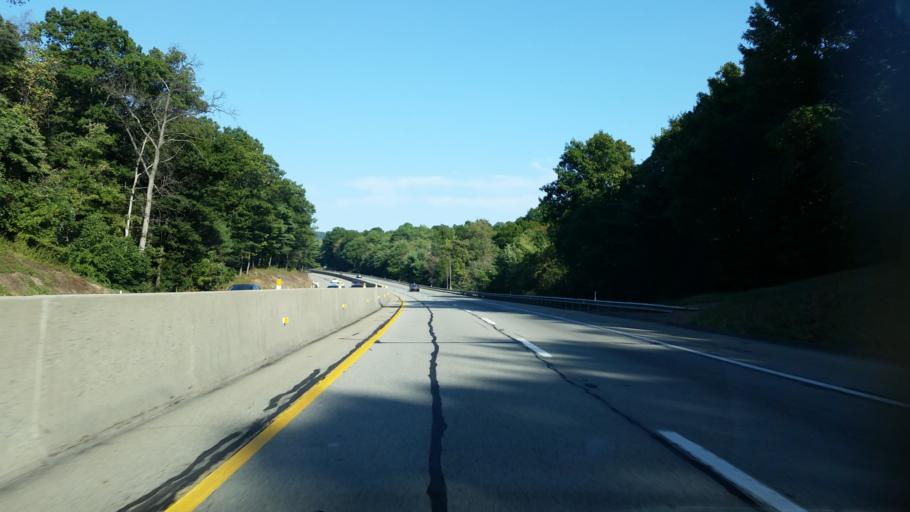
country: US
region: Pennsylvania
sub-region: Fulton County
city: McConnellsburg
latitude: 40.0372
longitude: -78.0003
